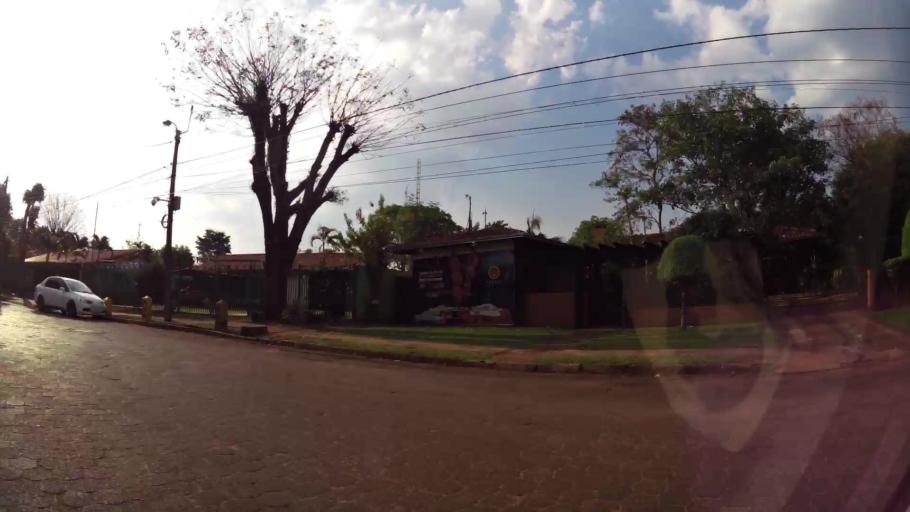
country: PY
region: Alto Parana
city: Presidente Franco
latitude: -25.5213
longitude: -54.6366
